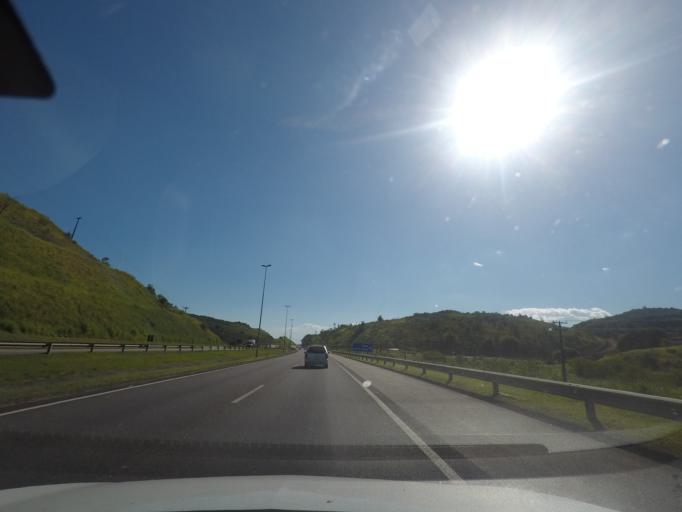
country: BR
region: Rio de Janeiro
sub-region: Guapimirim
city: Guapimirim
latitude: -22.6381
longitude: -43.0601
